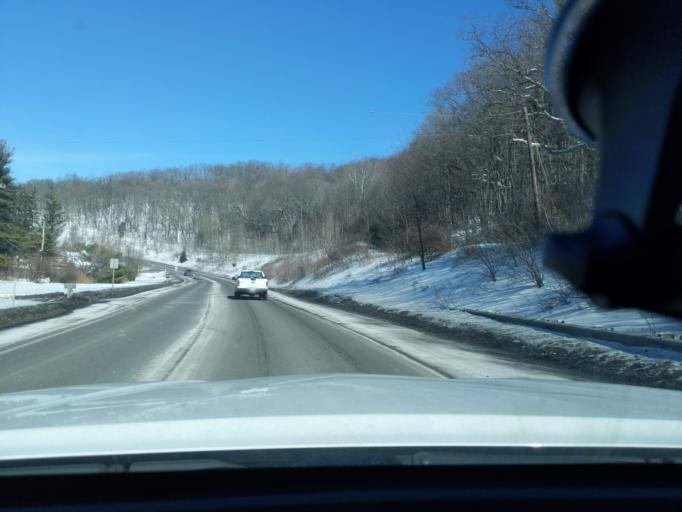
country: US
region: Maryland
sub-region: Allegany County
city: Lonaconing
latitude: 39.5830
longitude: -78.9501
